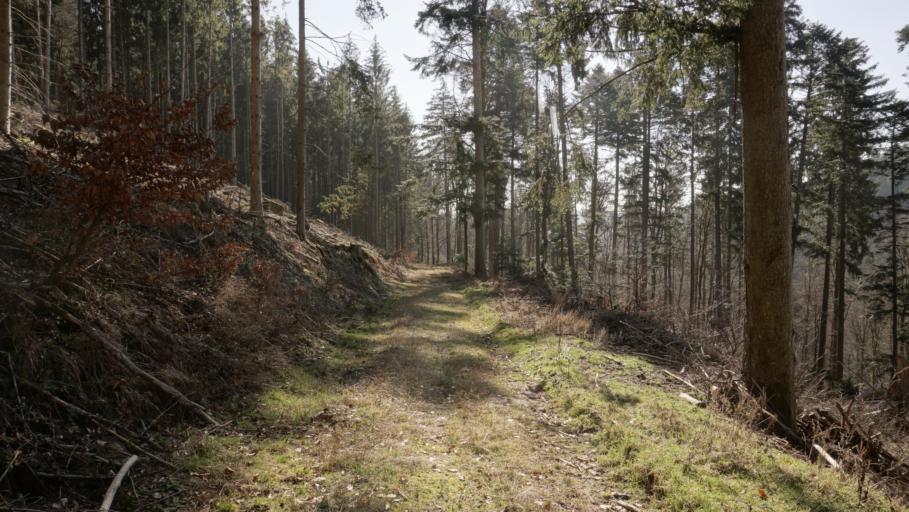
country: DE
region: Baden-Wuerttemberg
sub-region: Karlsruhe Region
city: Neckargerach
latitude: 49.4260
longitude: 9.0979
